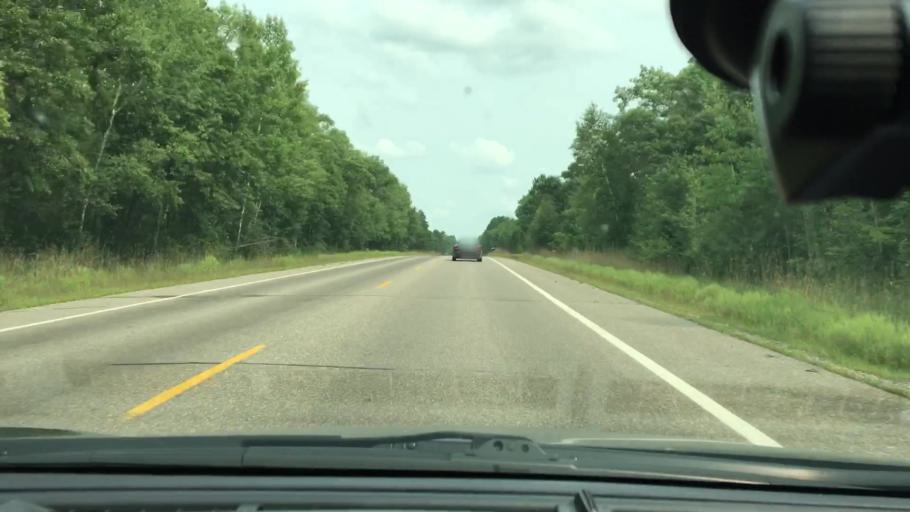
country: US
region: Minnesota
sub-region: Crow Wing County
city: Cross Lake
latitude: 46.7311
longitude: -94.0233
